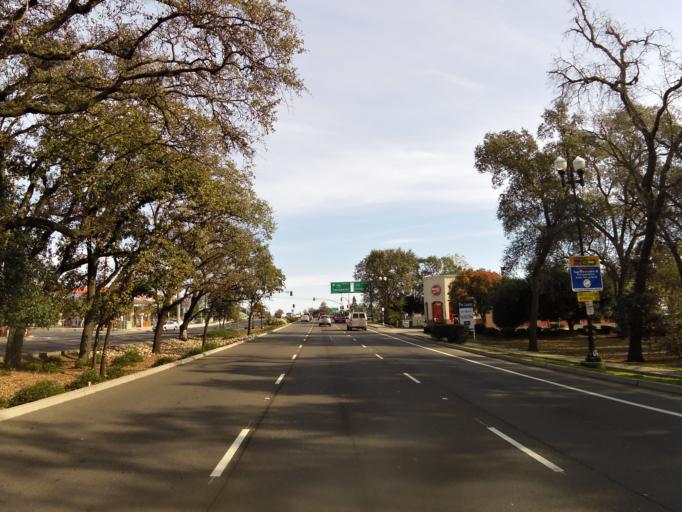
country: US
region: California
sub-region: Sacramento County
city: Elk Grove
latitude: 38.4090
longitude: -121.3914
